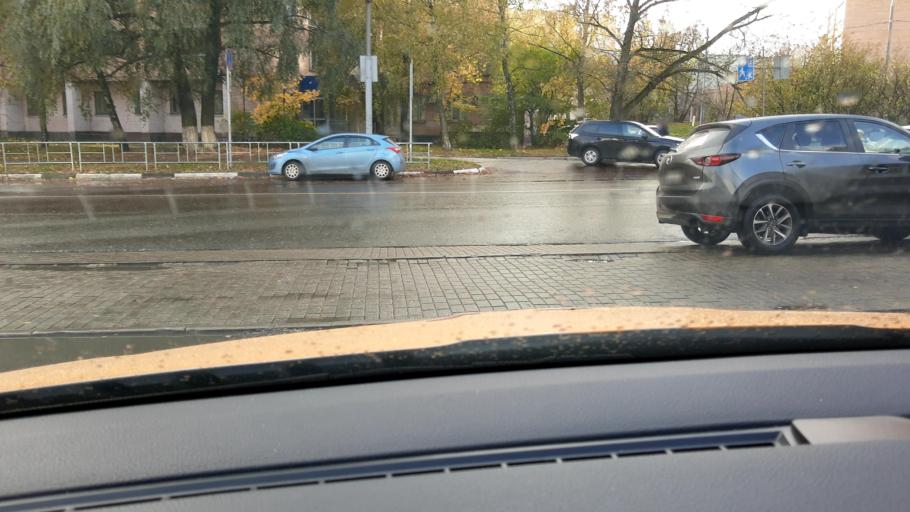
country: RU
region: Moskovskaya
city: Odintsovo
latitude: 55.6855
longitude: 37.2914
